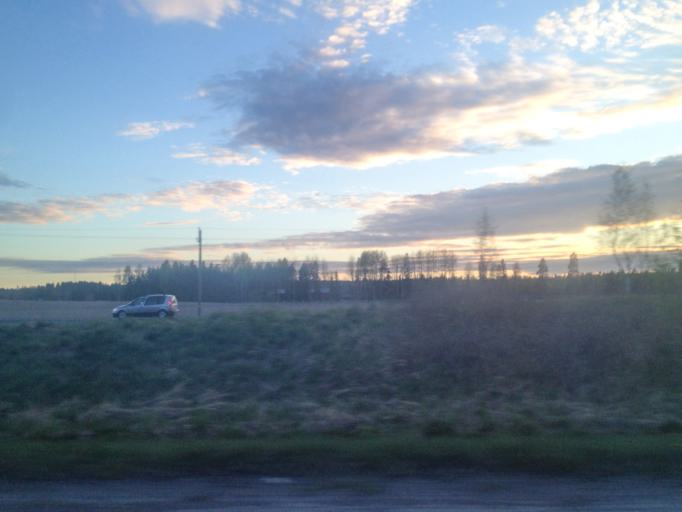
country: FI
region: Uusimaa
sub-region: Helsinki
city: Nurmijaervi
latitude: 60.4231
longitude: 24.8251
